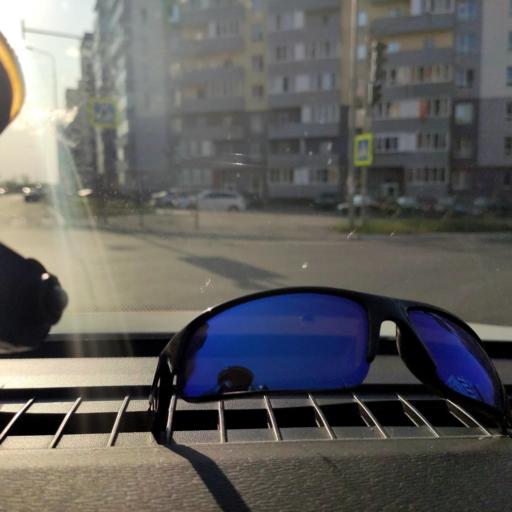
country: RU
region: Samara
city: Samara
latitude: 53.0936
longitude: 50.1620
